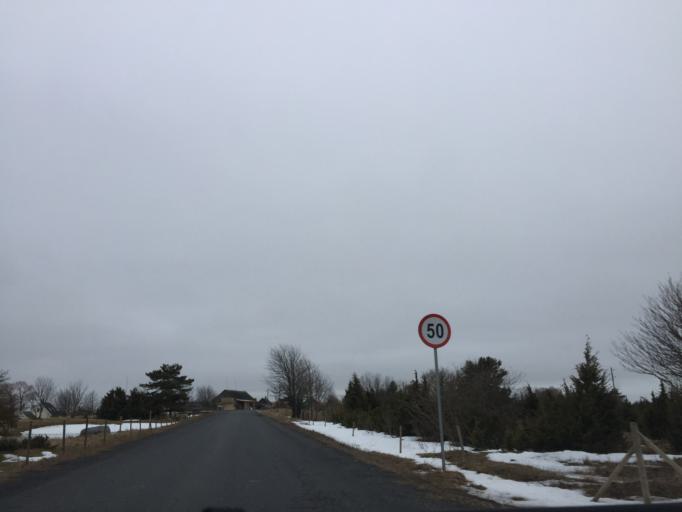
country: EE
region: Laeaene
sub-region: Haapsalu linn
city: Haapsalu
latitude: 58.7680
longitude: 23.4550
